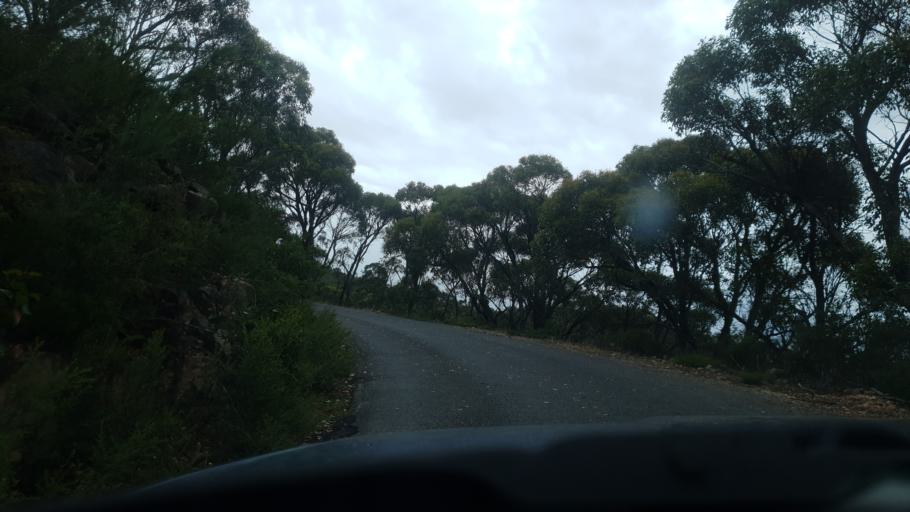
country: AU
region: Victoria
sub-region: Northern Grampians
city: Stawell
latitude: -37.2643
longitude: 142.5757
